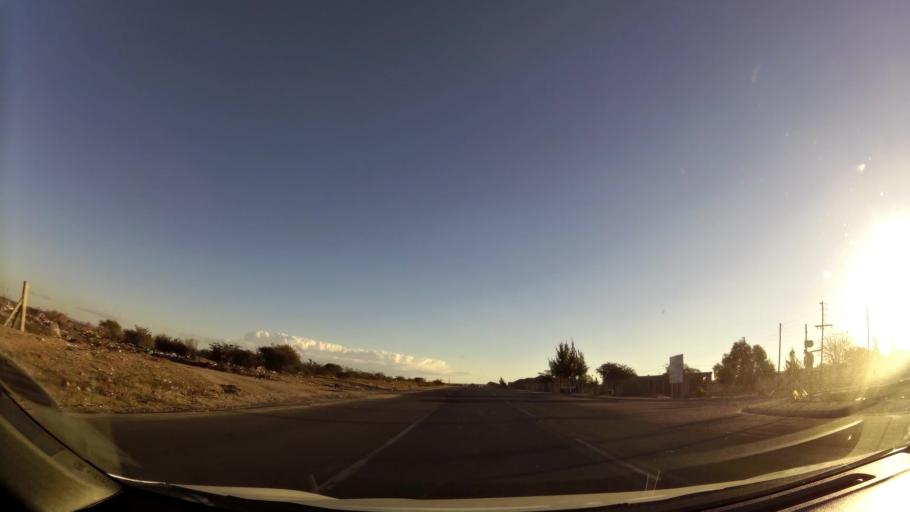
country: ZA
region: Limpopo
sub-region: Capricorn District Municipality
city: Polokwane
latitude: -23.8331
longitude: 29.3685
